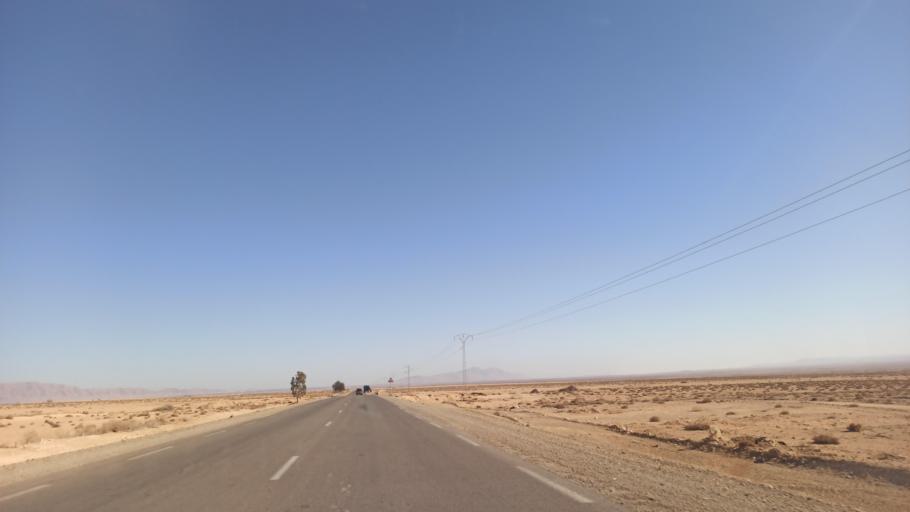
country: TN
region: Gafsa
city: Al Metlaoui
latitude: 34.3207
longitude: 8.5196
